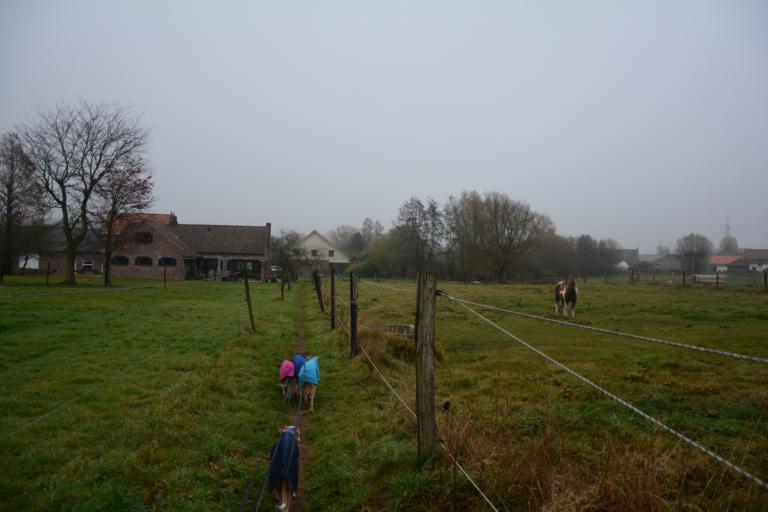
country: BE
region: Flanders
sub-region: Provincie Vlaams-Brabant
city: Wemmel
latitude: 50.8998
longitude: 4.2867
